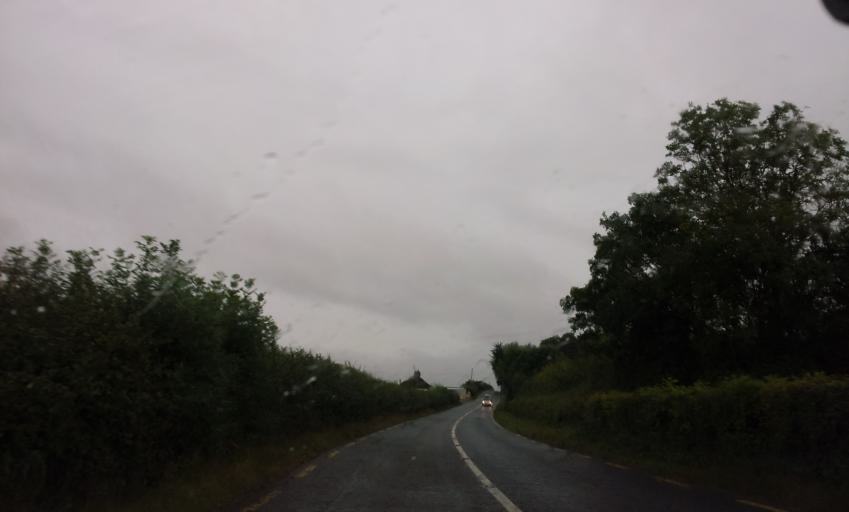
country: IE
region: Munster
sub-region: County Cork
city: Mallow
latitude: 52.1667
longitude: -8.5814
